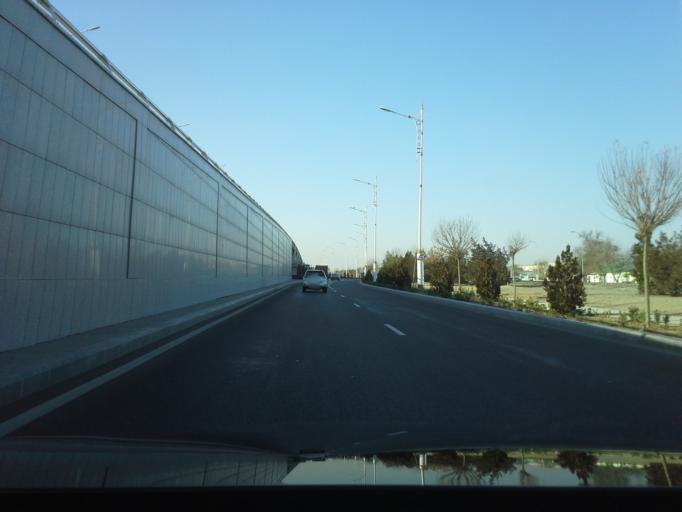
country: TM
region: Ahal
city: Ashgabat
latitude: 37.9613
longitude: 58.3642
